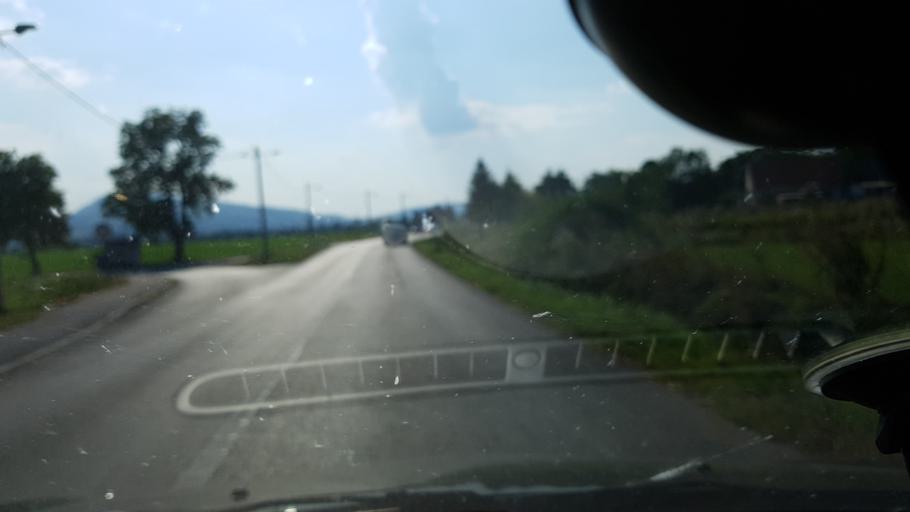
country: HR
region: Zagrebacka
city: Bregana
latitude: 45.8844
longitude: 15.7110
